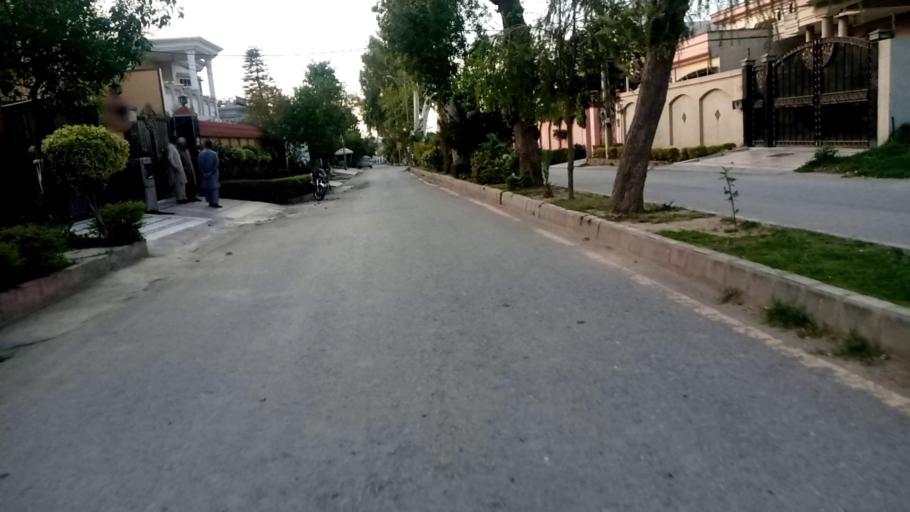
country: PK
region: Khyber Pakhtunkhwa
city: Peshawar
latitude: 34.0215
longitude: 71.5509
